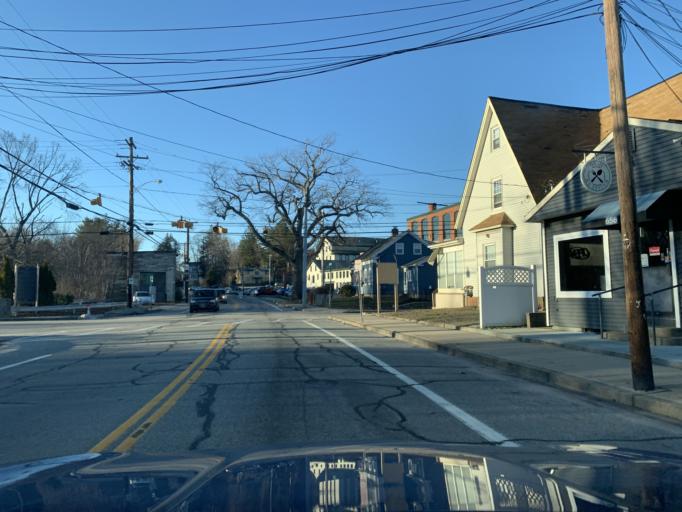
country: US
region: Rhode Island
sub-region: Kent County
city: West Warwick
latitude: 41.7240
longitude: -71.5352
